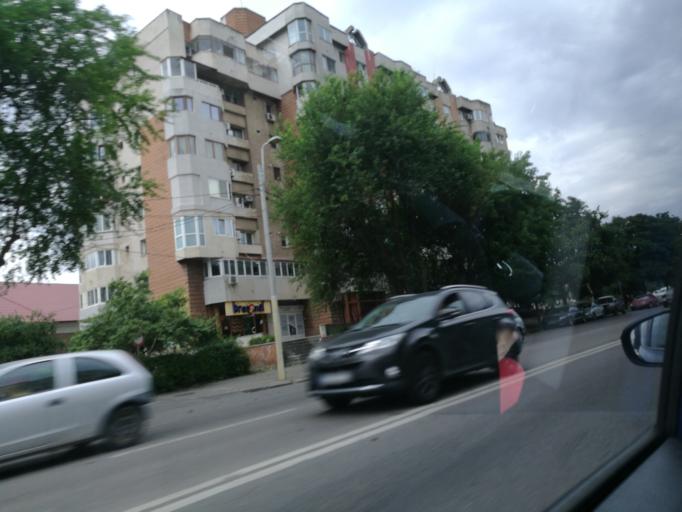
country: RO
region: Constanta
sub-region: Municipiul Constanta
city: Constanta
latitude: 44.1662
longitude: 28.6338
